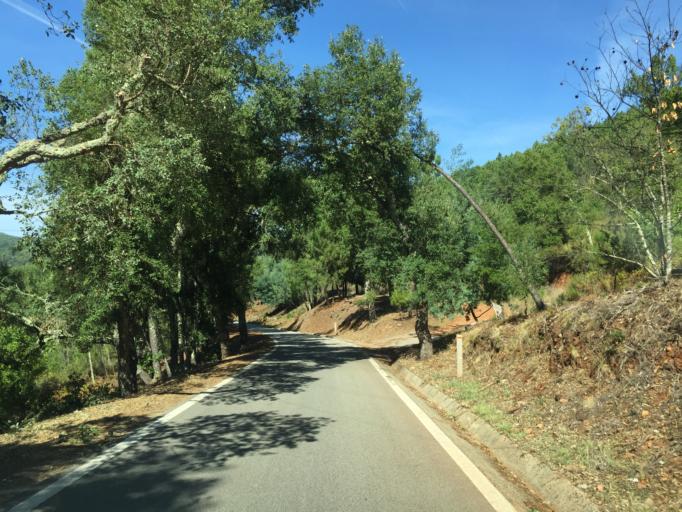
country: PT
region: Portalegre
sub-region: Marvao
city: Marvao
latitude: 39.3758
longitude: -7.3838
